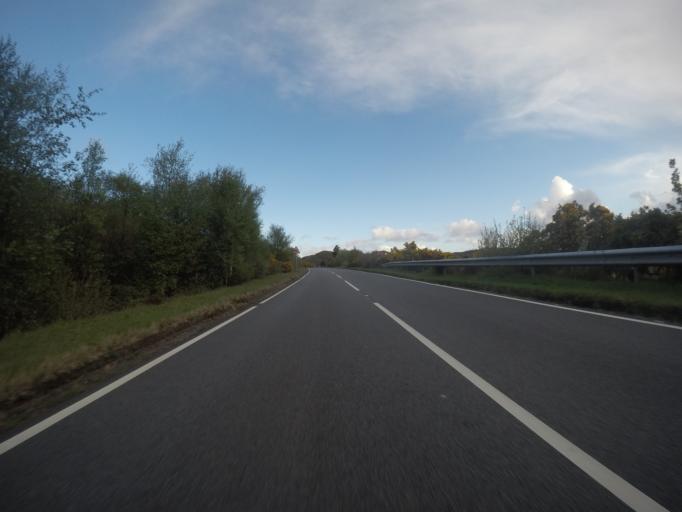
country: GB
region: Scotland
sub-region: Highland
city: Portree
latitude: 57.5218
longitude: -6.3419
